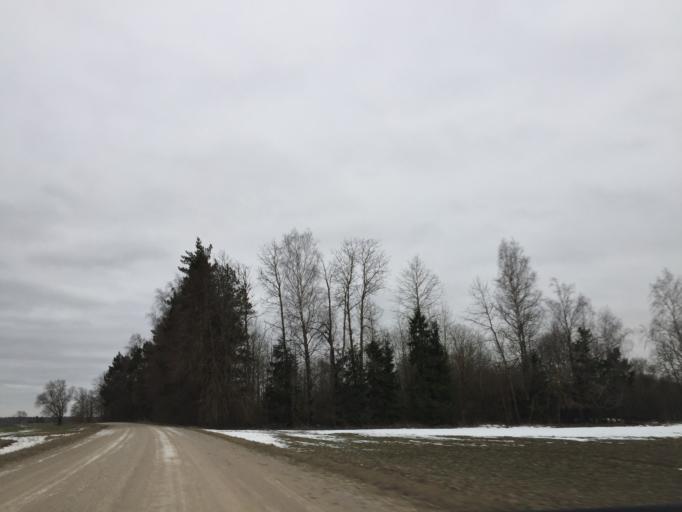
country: LT
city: Zagare
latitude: 56.2863
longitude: 23.2589
